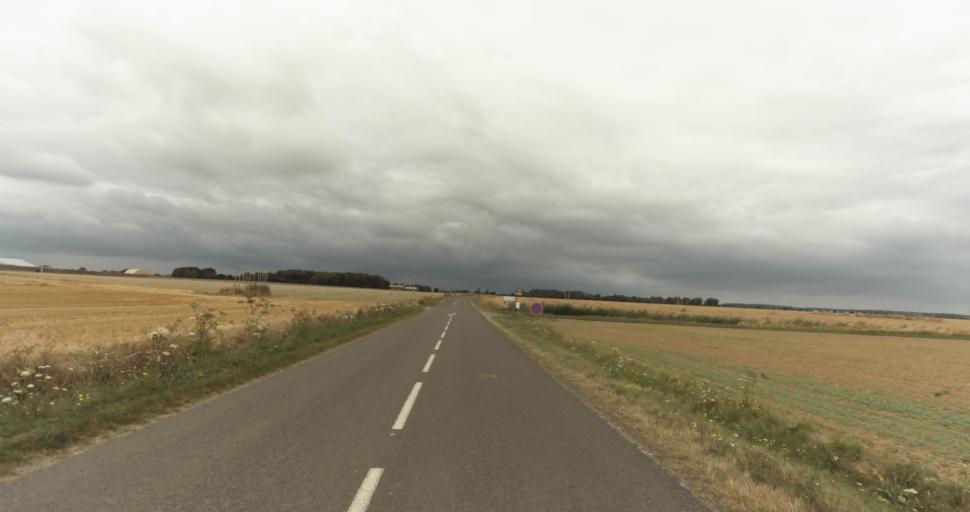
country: FR
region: Haute-Normandie
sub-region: Departement de l'Eure
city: Gravigny
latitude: 49.0408
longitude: 1.2368
